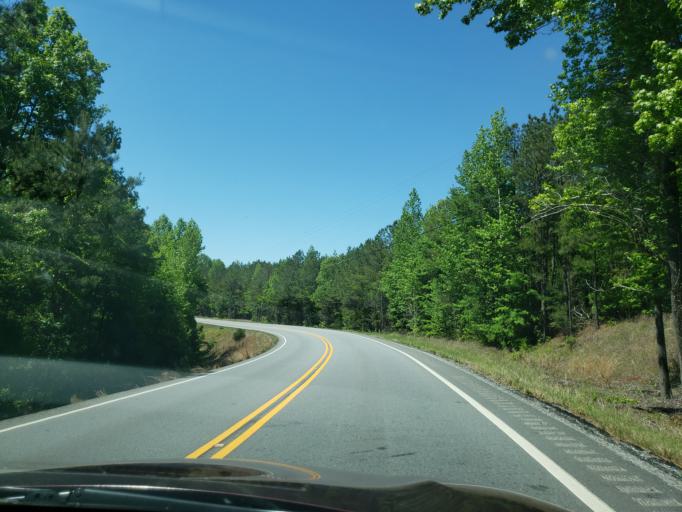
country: US
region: Alabama
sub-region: Tallapoosa County
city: Dadeville
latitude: 32.6698
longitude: -85.7935
